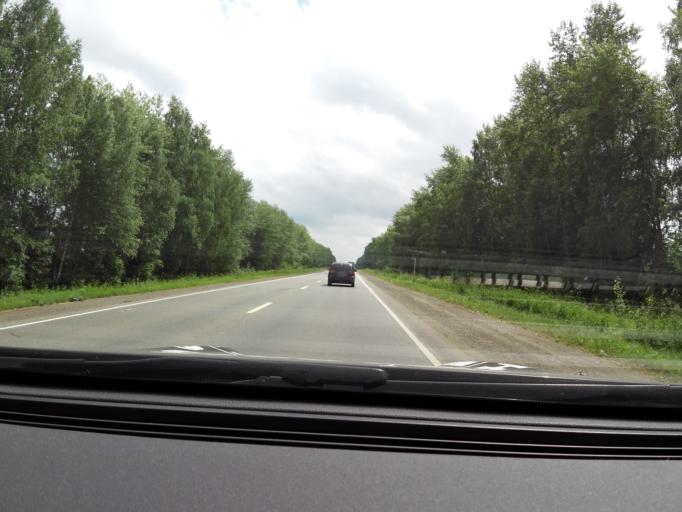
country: RU
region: Perm
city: Kukushtan
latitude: 57.6178
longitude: 56.4876
